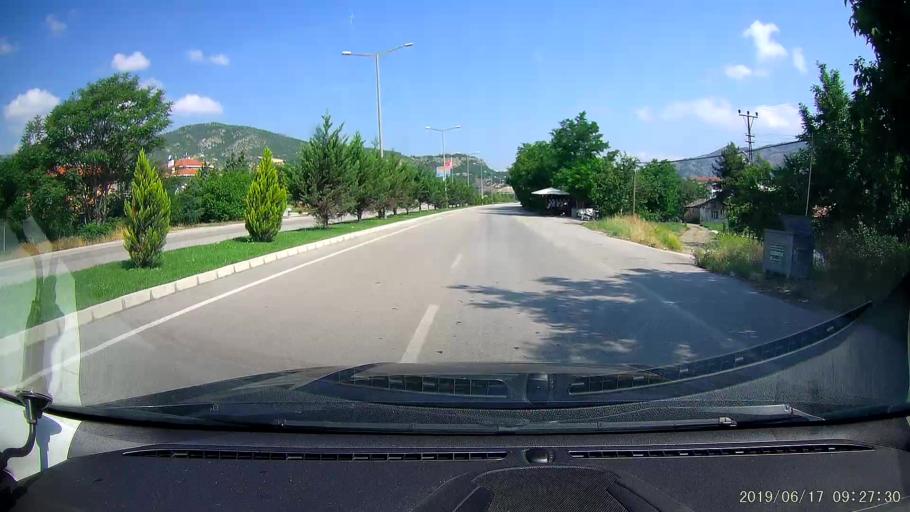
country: TR
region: Amasya
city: Amasya
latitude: 40.6778
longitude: 35.8260
